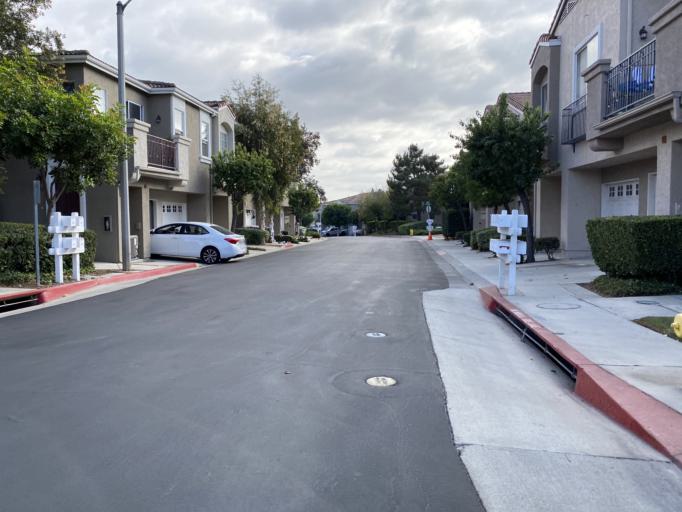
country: US
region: California
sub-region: Orange County
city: Yorba Linda
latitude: 33.8729
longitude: -117.8326
